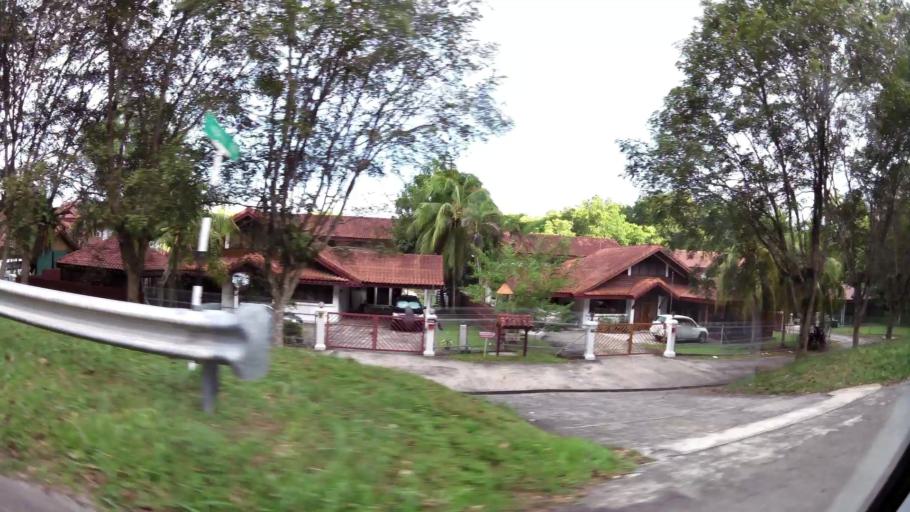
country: BN
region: Brunei and Muara
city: Bandar Seri Begawan
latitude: 4.9059
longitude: 114.9946
